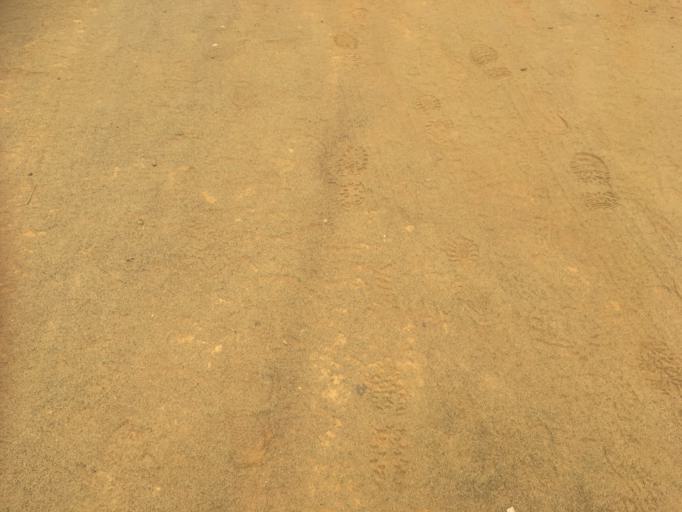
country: US
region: Hawaii
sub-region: Hawaii County
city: Hawaiian Ocean View
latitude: 18.9198
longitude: -155.6642
